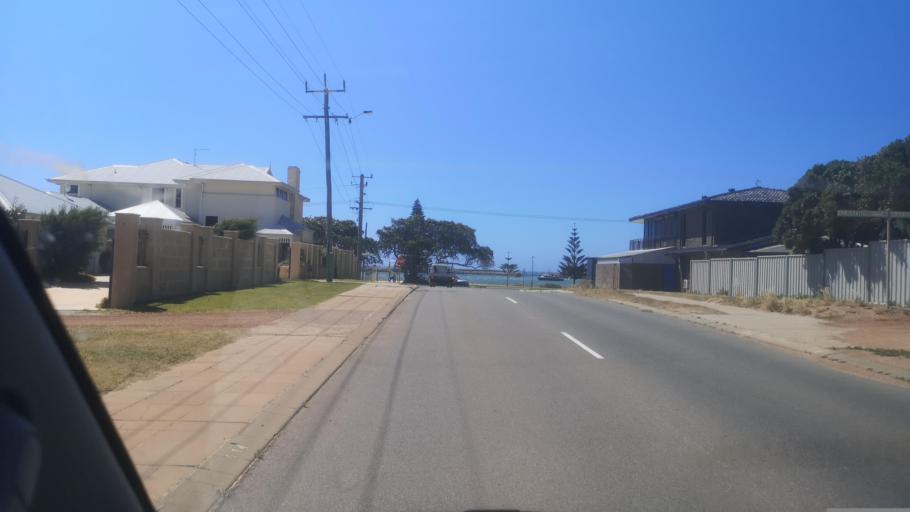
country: AU
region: Western Australia
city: Port Denison
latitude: -29.2772
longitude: 114.9179
